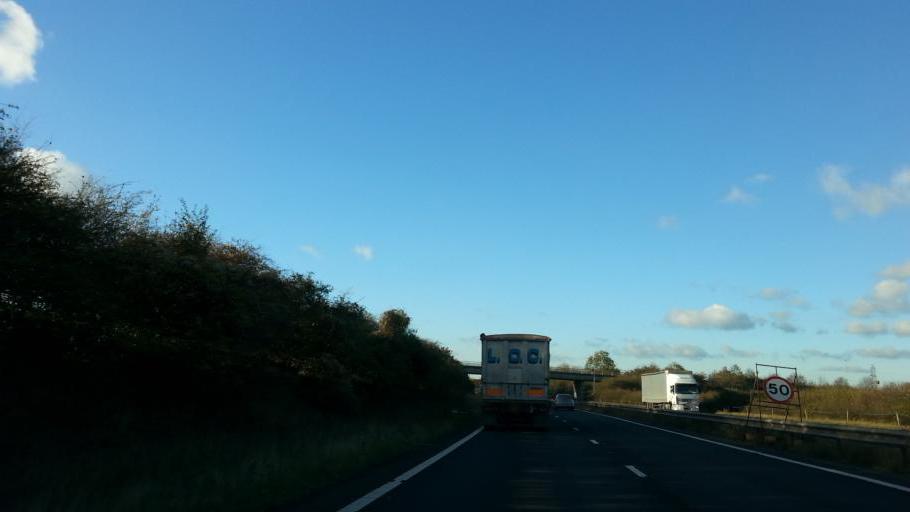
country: GB
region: England
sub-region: Cambridgeshire
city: Waterbeach
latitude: 52.2276
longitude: 0.1814
